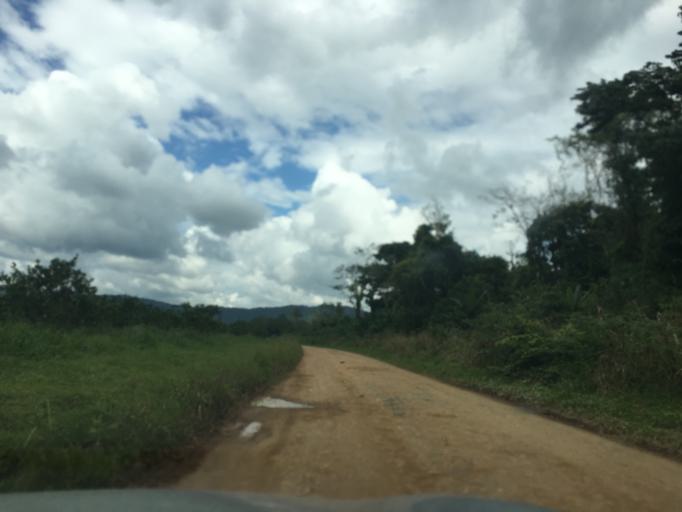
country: BZ
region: Stann Creek
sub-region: Dangriga
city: Dangriga
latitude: 16.9207
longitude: -88.3474
